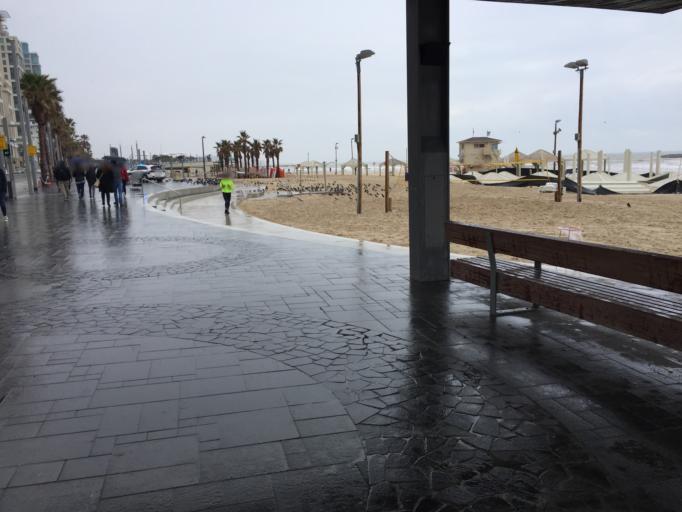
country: IL
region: Tel Aviv
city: Tel Aviv
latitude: 32.0743
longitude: 34.7651
